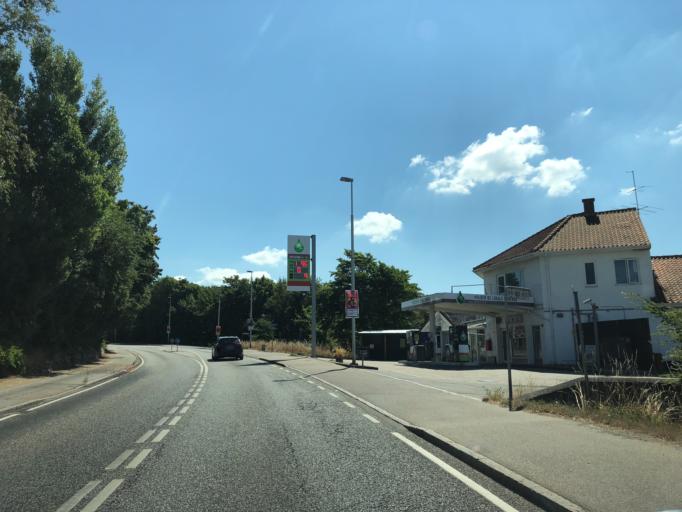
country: DK
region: Capital Region
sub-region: Halsnaes Kommune
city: Hundested
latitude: 55.9634
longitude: 11.8577
